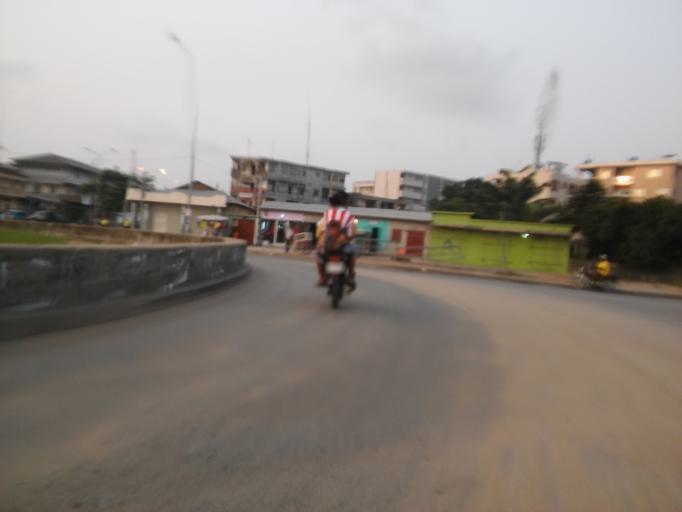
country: BJ
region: Littoral
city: Cotonou
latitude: 6.3631
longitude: 2.4470
